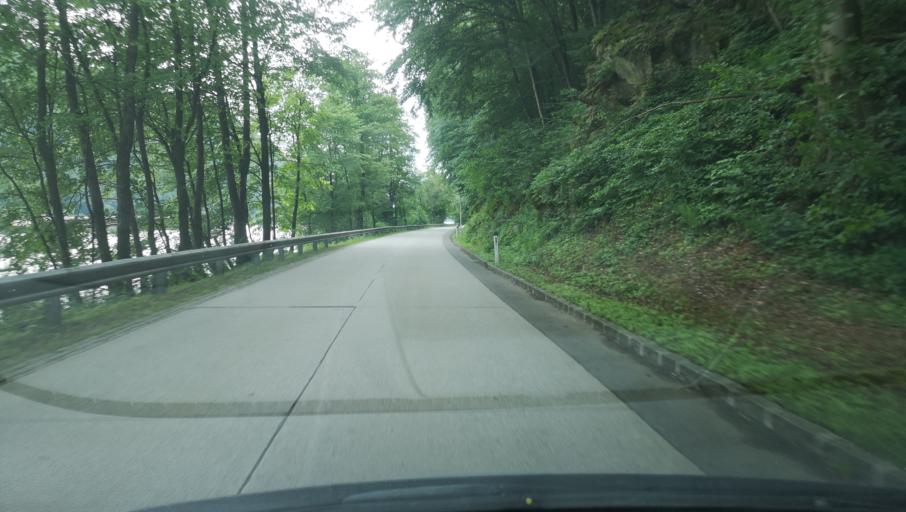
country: AT
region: Lower Austria
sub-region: Politischer Bezirk Melk
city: Nochling
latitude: 48.1938
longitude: 14.9981
